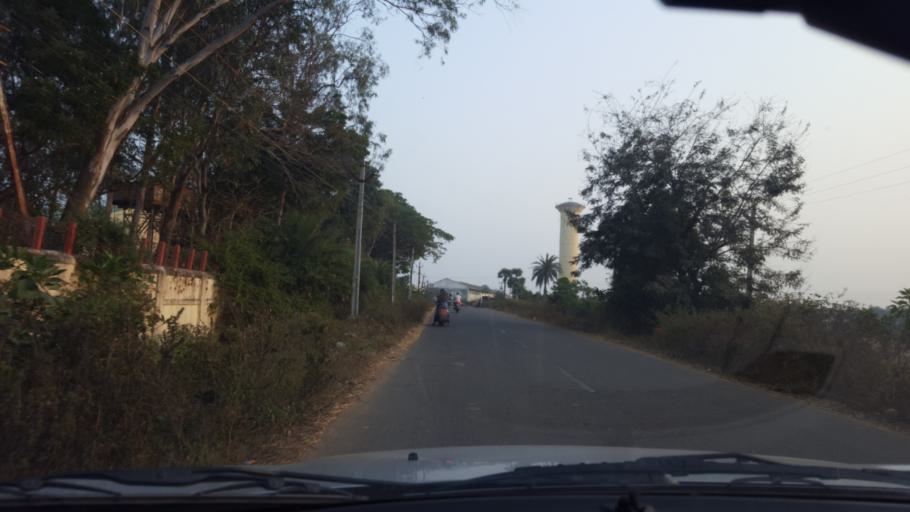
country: IN
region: Andhra Pradesh
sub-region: Srikakulam
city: Amudalavalasa
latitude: 18.3862
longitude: 83.9233
